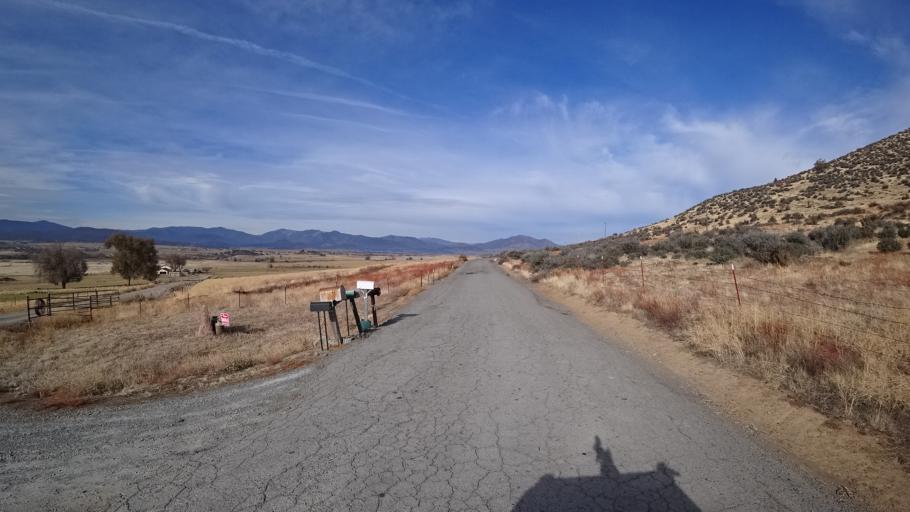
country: US
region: California
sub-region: Siskiyou County
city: Montague
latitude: 41.7094
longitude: -122.5190
